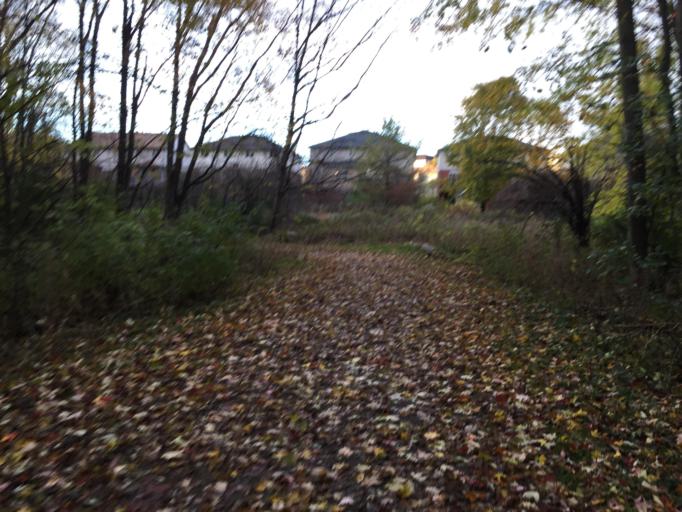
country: CA
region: Ontario
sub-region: Wellington County
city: Guelph
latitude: 43.5275
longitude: -80.3035
